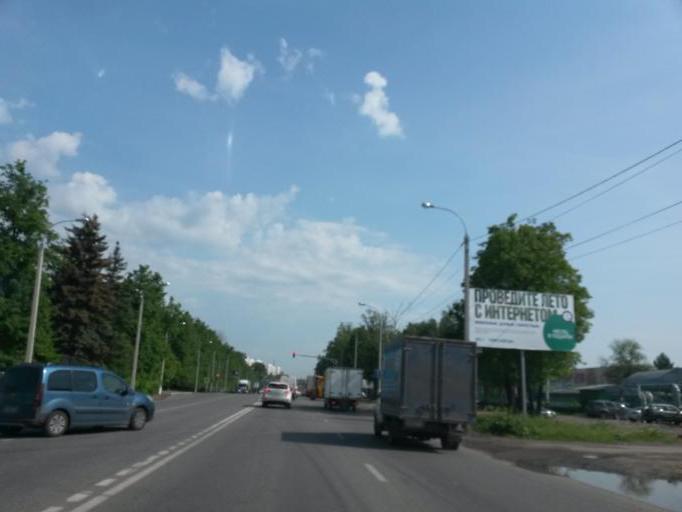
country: RU
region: Moskovskaya
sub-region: Chekhovskiy Rayon
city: Chekhov
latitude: 55.1597
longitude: 37.4650
